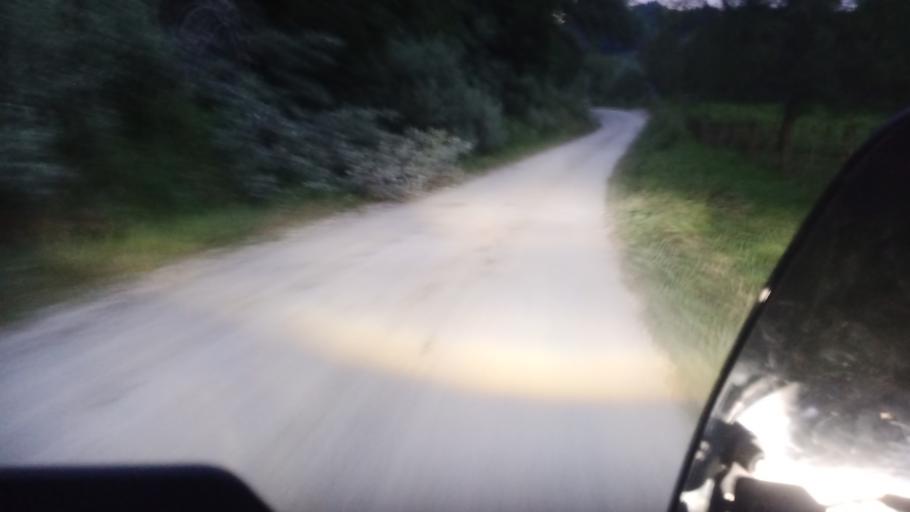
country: NZ
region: Gisborne
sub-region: Gisborne District
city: Gisborne
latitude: -38.4923
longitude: 177.9593
